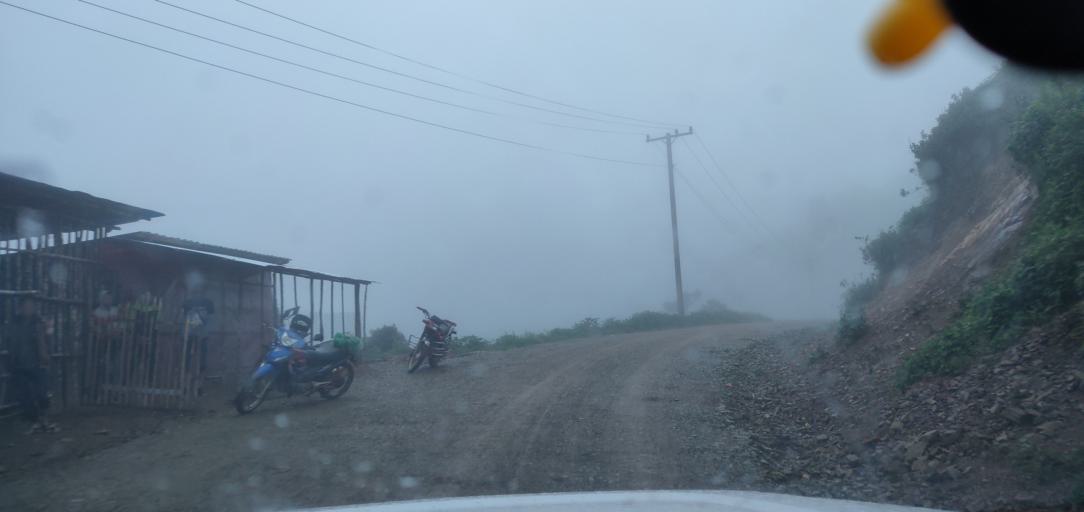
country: LA
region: Phongsali
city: Phongsali
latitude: 21.3907
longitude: 102.1932
